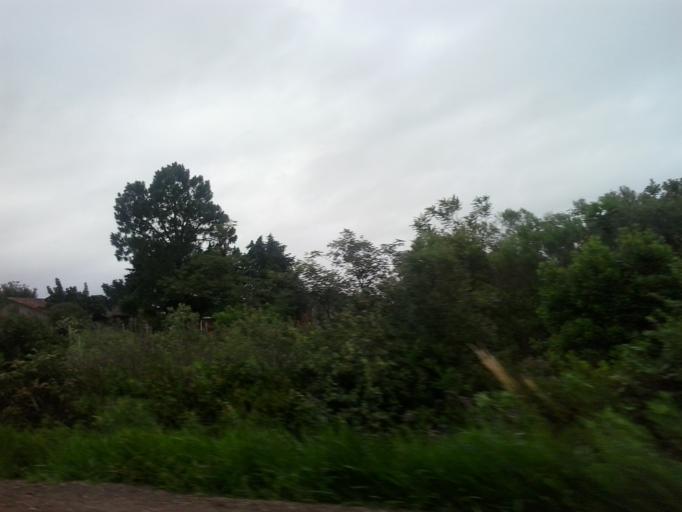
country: BR
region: Rio Grande do Sul
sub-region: Santa Maria
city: Santa Maria
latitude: -29.7223
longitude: -53.3789
